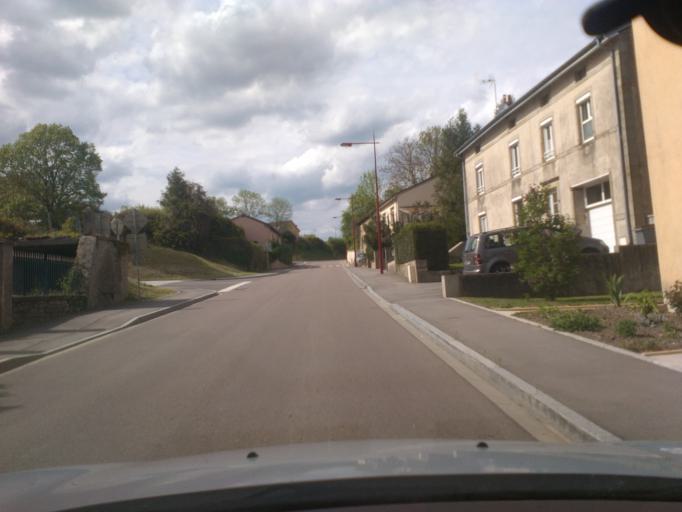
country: FR
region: Lorraine
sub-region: Departement des Vosges
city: Mirecourt
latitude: 48.2663
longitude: 6.1418
